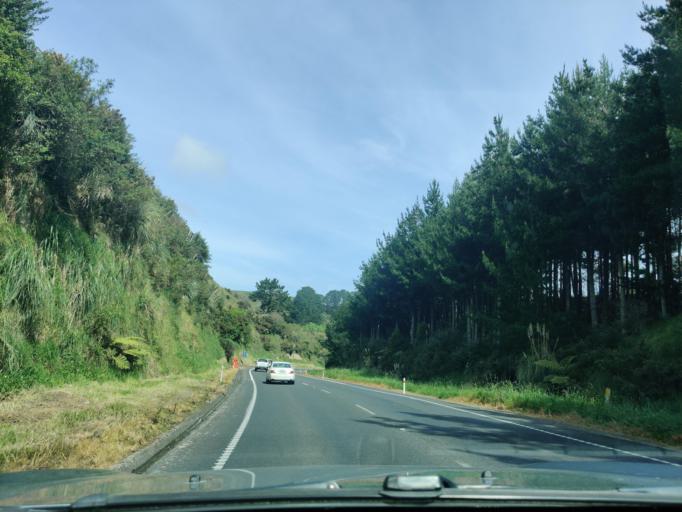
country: NZ
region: Taranaki
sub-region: South Taranaki District
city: Hawera
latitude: -39.6376
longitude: 174.3764
